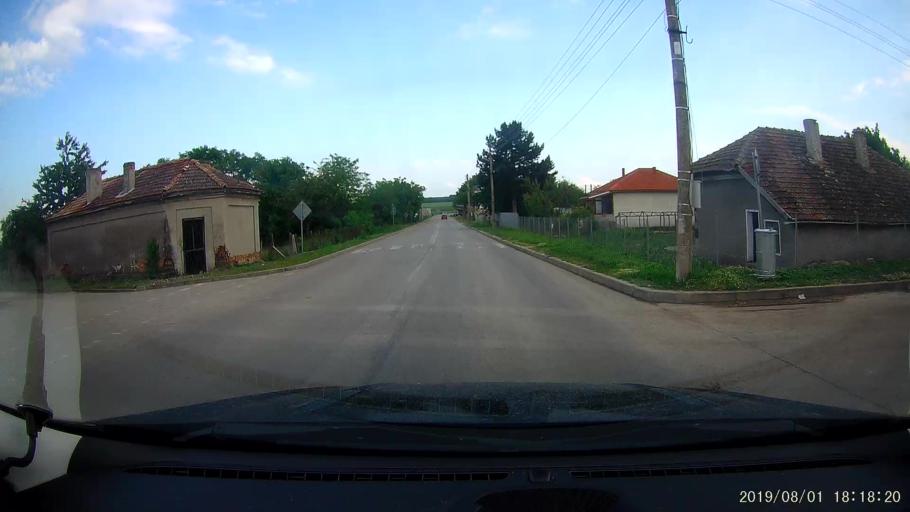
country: BG
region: Shumen
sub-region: Obshtina Kaolinovo
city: Kaolinovo
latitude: 43.6992
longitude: 27.0806
